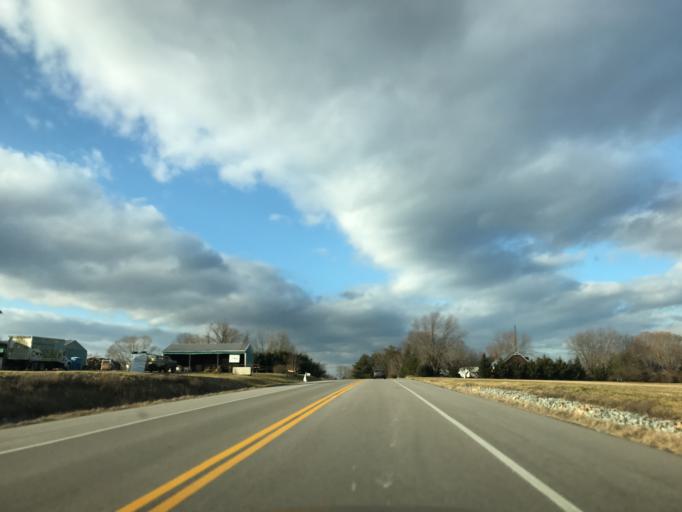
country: US
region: Maryland
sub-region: Cecil County
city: Rising Sun
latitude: 39.6657
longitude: -76.0153
